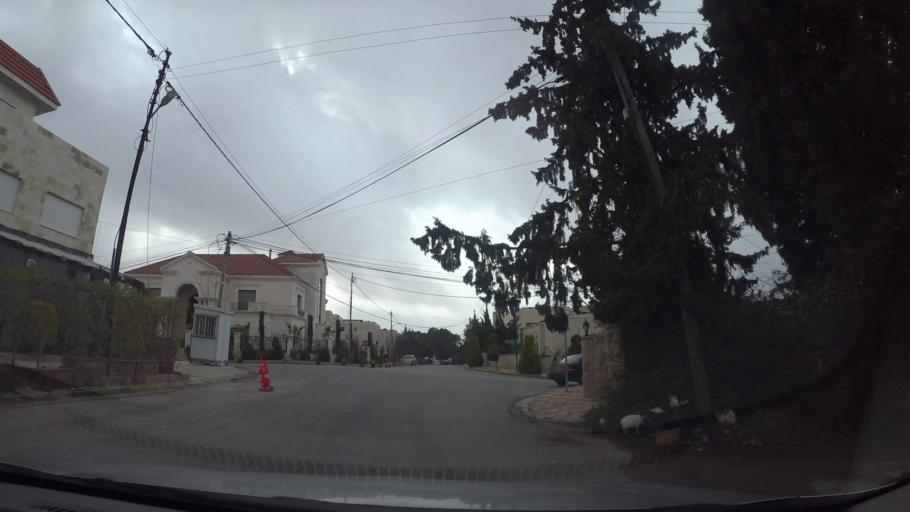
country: JO
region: Amman
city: Wadi as Sir
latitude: 31.9884
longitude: 35.8180
